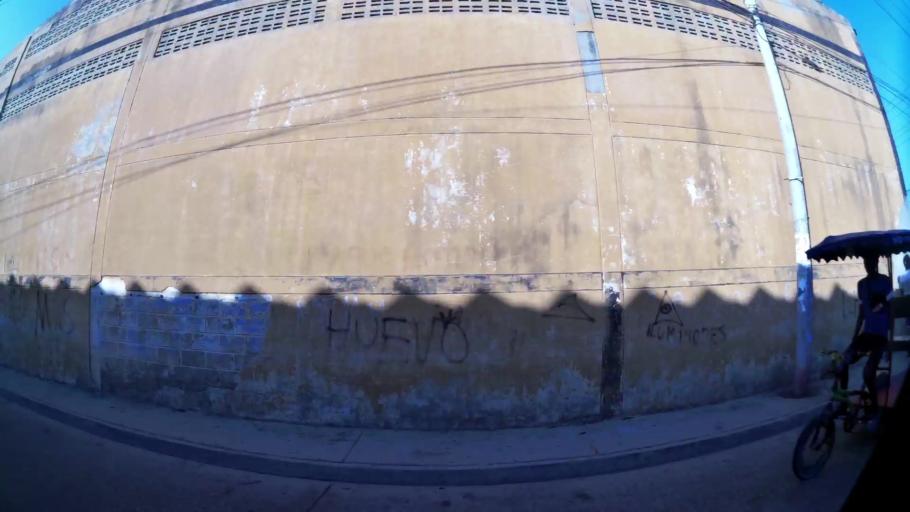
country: CO
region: Atlantico
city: Barranquilla
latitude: 11.0396
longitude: -74.8242
